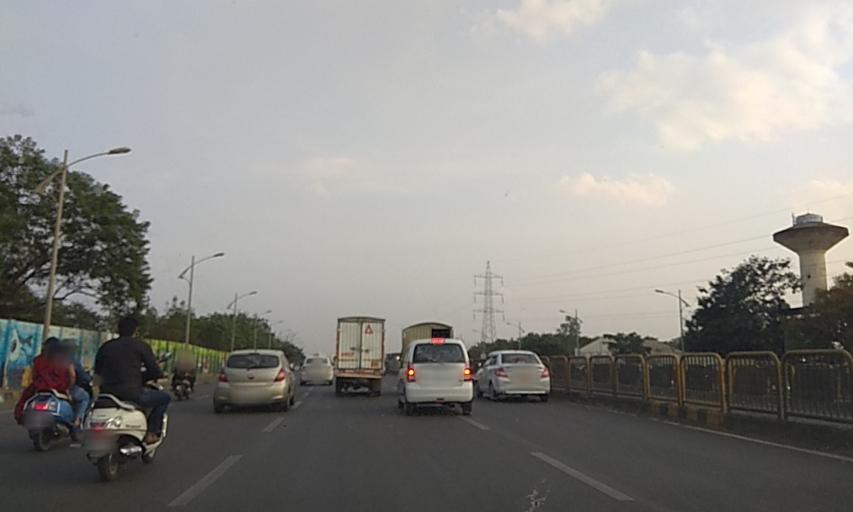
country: IN
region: Maharashtra
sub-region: Pune Division
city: Pimpri
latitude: 18.5809
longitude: 73.7991
